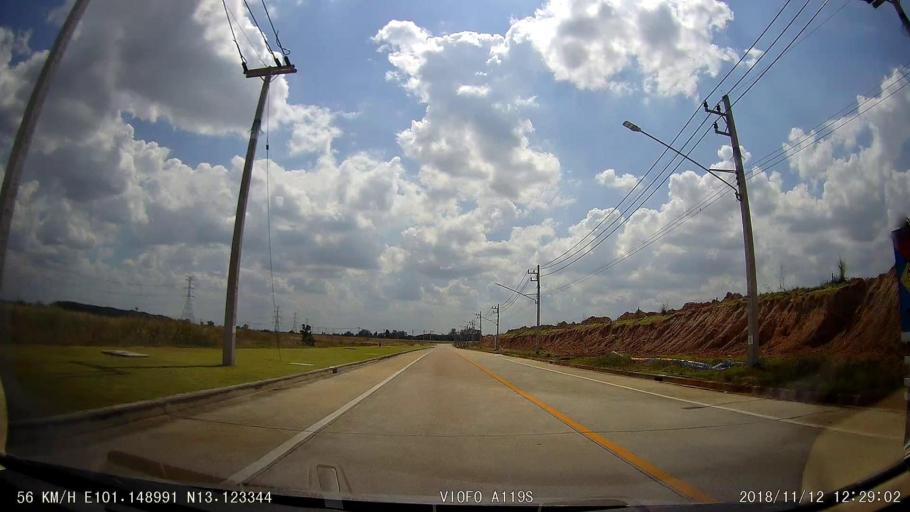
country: TH
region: Chon Buri
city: Ban Talat Bueng
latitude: 13.1229
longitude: 101.1490
